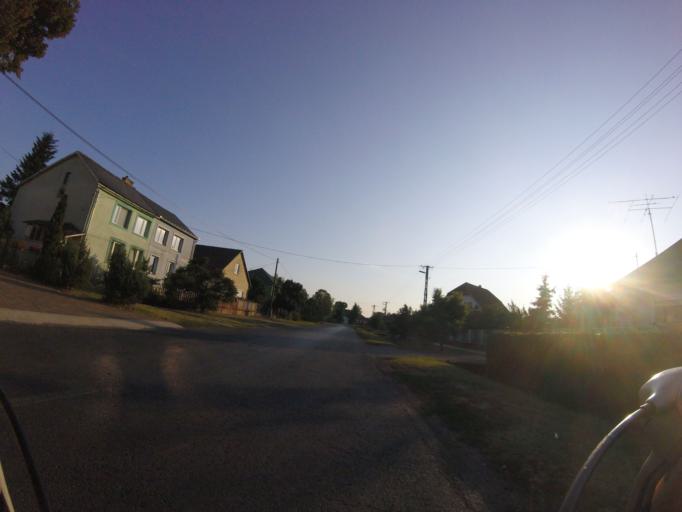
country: HU
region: Szabolcs-Szatmar-Bereg
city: Nyirtelek
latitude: 48.0123
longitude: 21.6436
